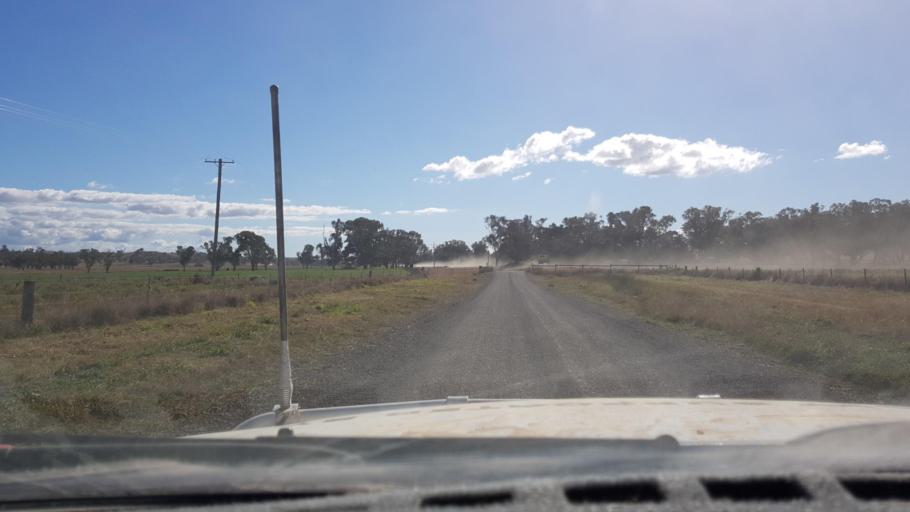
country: AU
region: New South Wales
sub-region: Narrabri
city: Blair Athol
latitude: -30.5220
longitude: 150.4441
